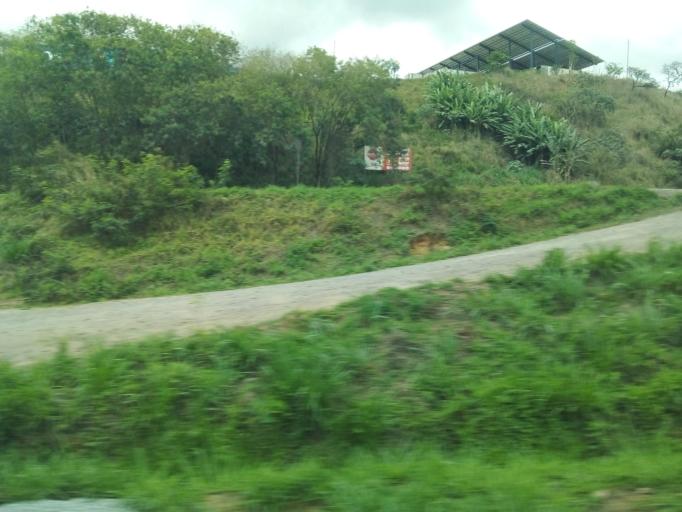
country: BR
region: Minas Gerais
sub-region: Coronel Fabriciano
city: Coronel Fabriciano
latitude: -19.5320
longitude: -42.6719
